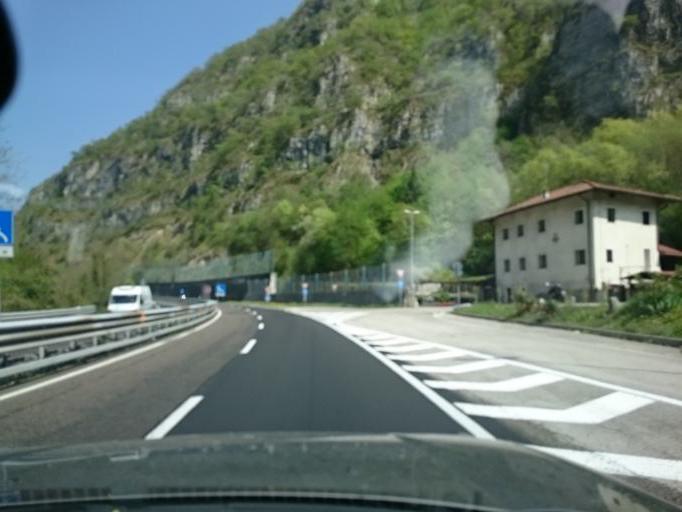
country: IT
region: Veneto
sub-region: Provincia di Vicenza
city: Valstagna
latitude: 45.8724
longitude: 11.6747
